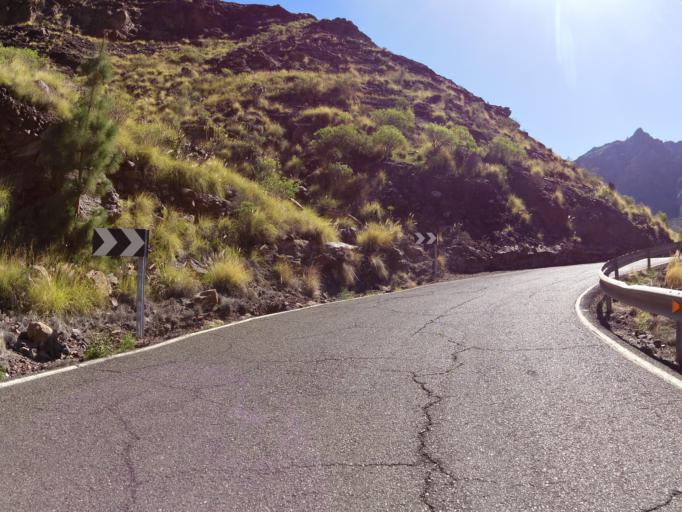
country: ES
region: Canary Islands
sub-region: Provincia de Las Palmas
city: San Nicolas
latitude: 27.9837
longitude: -15.7317
